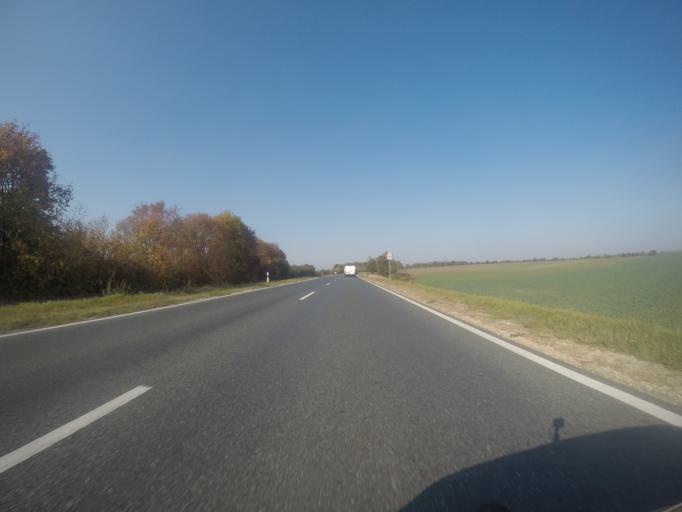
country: HU
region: Tolna
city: Bolcske
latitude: 46.7293
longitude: 18.8829
